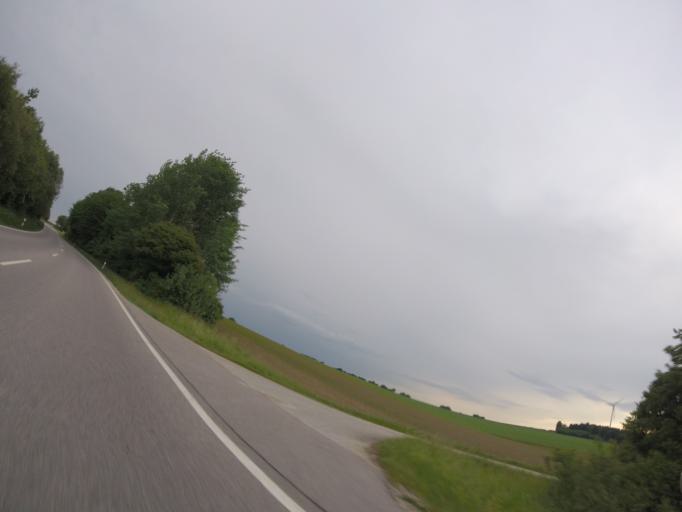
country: DE
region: Bavaria
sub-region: Upper Bavaria
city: Hohenkammer
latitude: 48.3887
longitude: 11.5390
